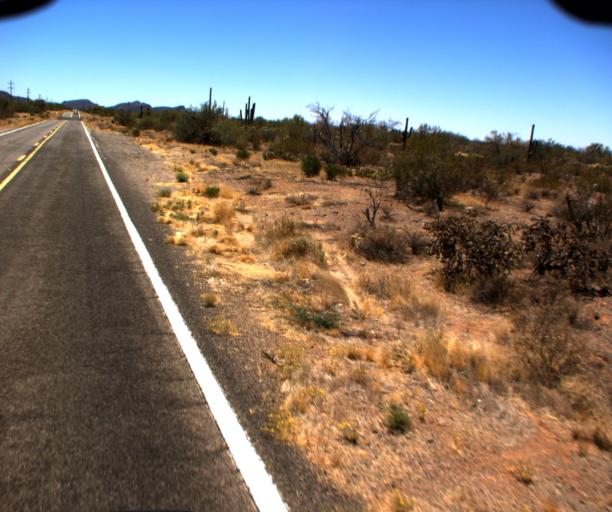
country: US
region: Arizona
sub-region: Pima County
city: Sells
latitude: 32.0169
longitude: -111.9988
